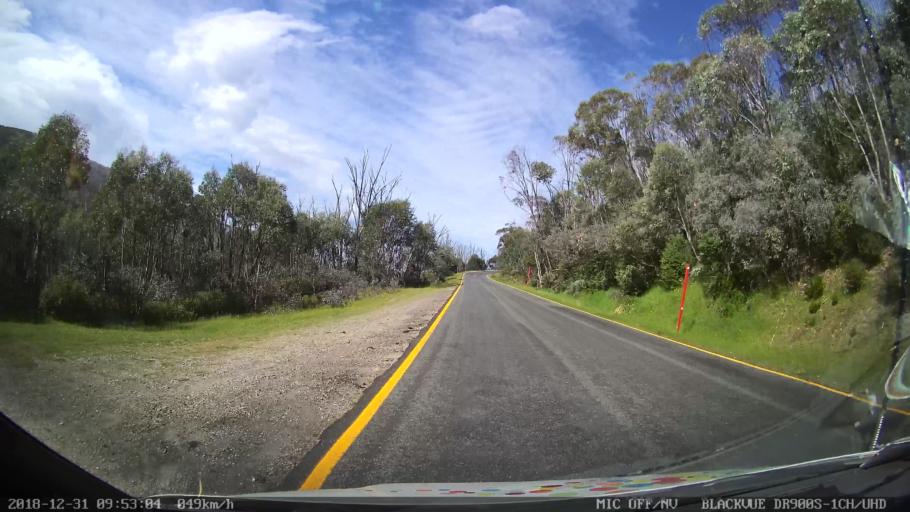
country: AU
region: New South Wales
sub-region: Snowy River
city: Jindabyne
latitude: -36.5285
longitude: 148.2469
